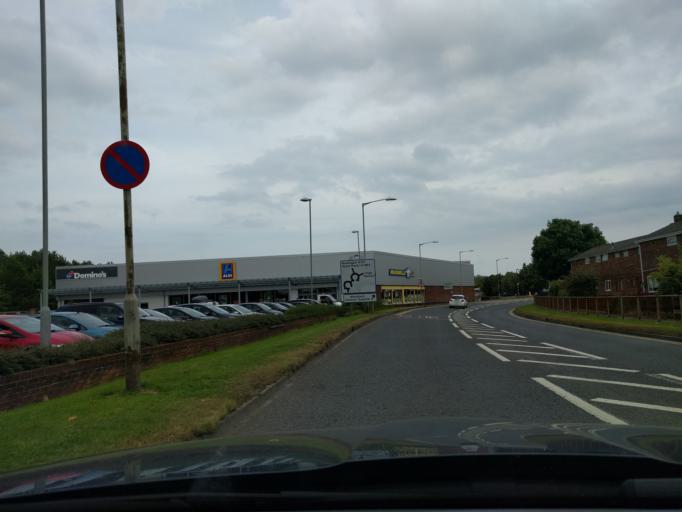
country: GB
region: England
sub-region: Northumberland
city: Ashington
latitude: 55.1852
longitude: -1.5886
